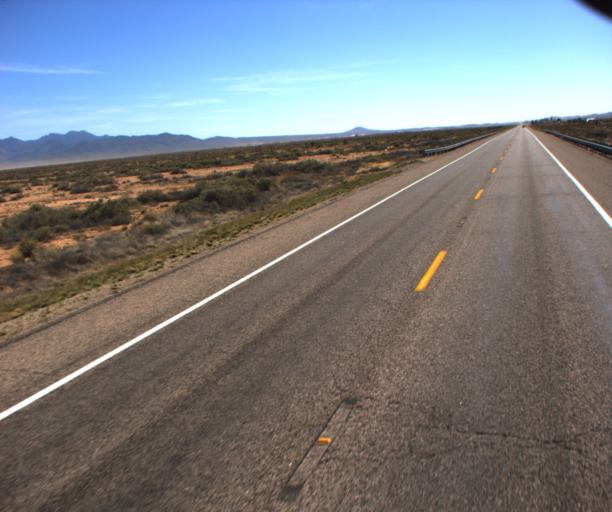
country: US
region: Arizona
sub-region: Mohave County
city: New Kingman-Butler
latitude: 35.3166
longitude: -113.9157
